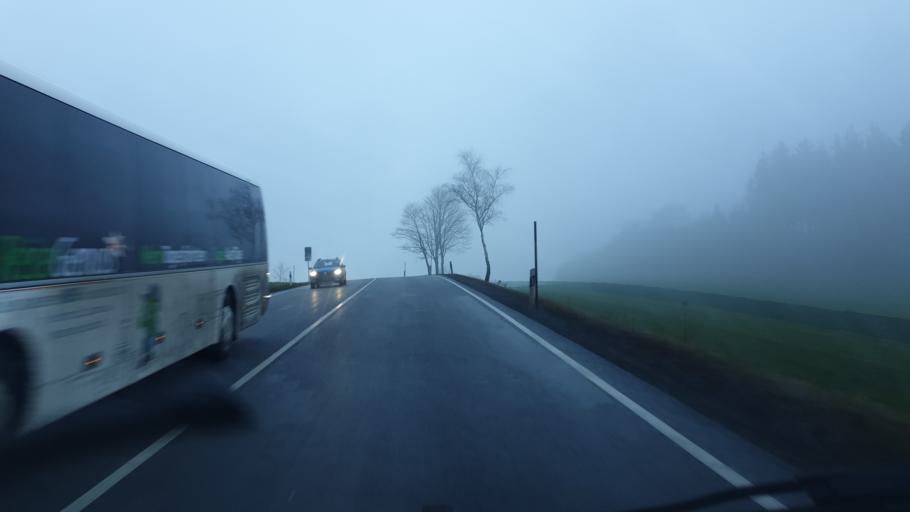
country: DE
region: Saxony
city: Grossolbersdorf
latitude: 50.6952
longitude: 13.1117
